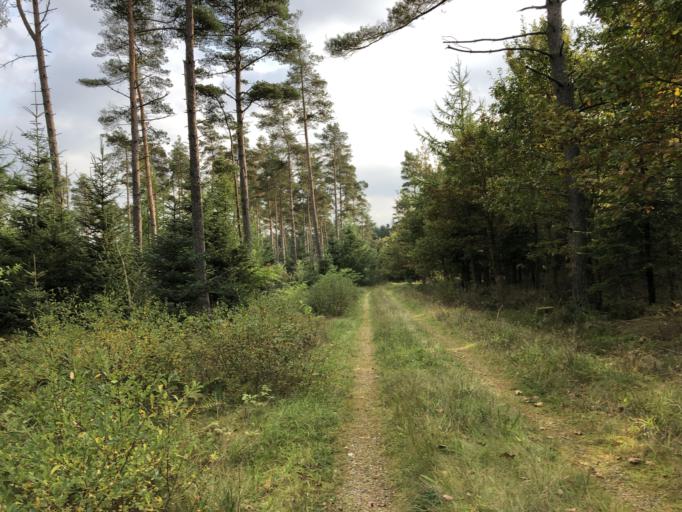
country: DK
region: Central Jutland
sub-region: Holstebro Kommune
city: Ulfborg
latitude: 56.2151
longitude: 8.4384
